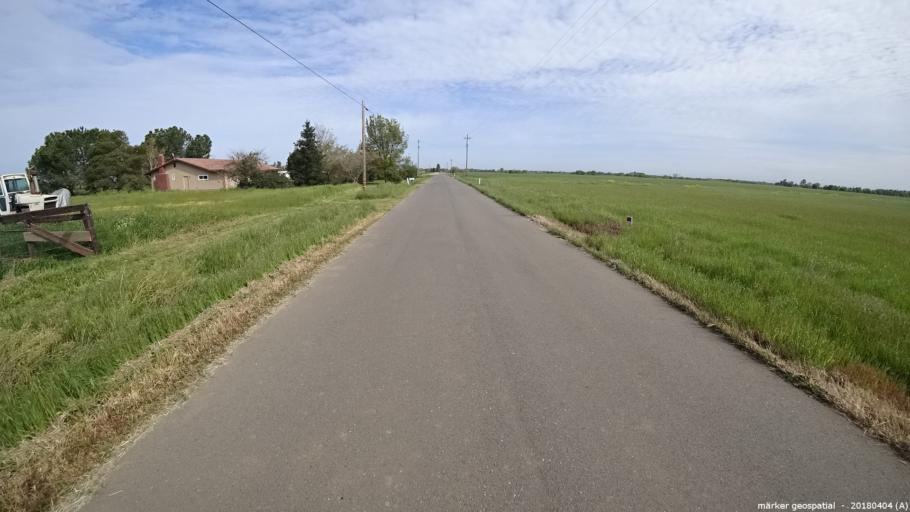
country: US
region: California
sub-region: Sacramento County
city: Herald
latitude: 38.2978
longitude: -121.2772
